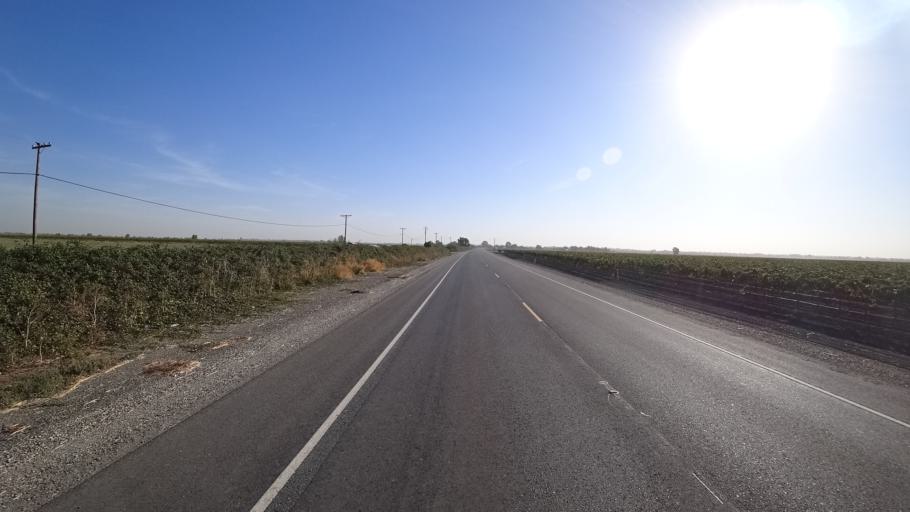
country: US
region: California
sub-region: Sacramento County
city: Parkway
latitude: 38.4145
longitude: -121.5758
